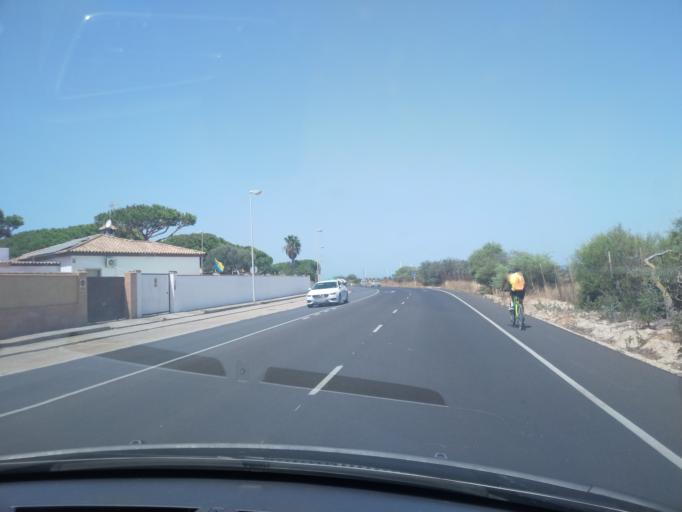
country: ES
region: Andalusia
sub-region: Provincia de Cadiz
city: Chiclana de la Frontera
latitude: 36.3848
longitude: -6.1994
